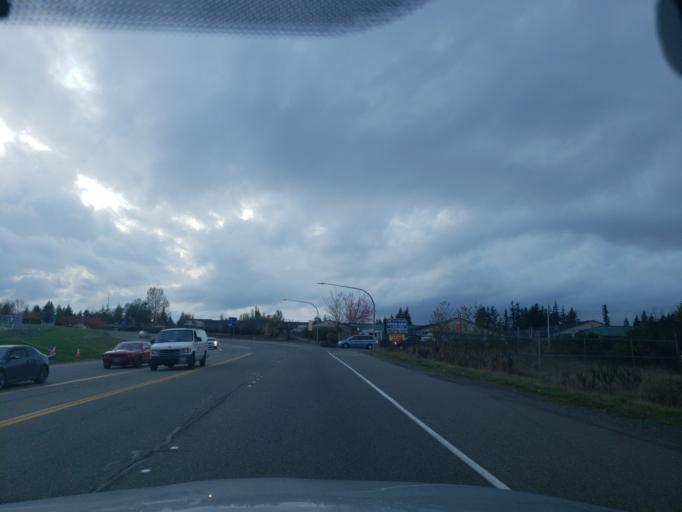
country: US
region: Washington
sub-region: Snohomish County
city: Mukilteo
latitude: 47.9246
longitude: -122.2869
